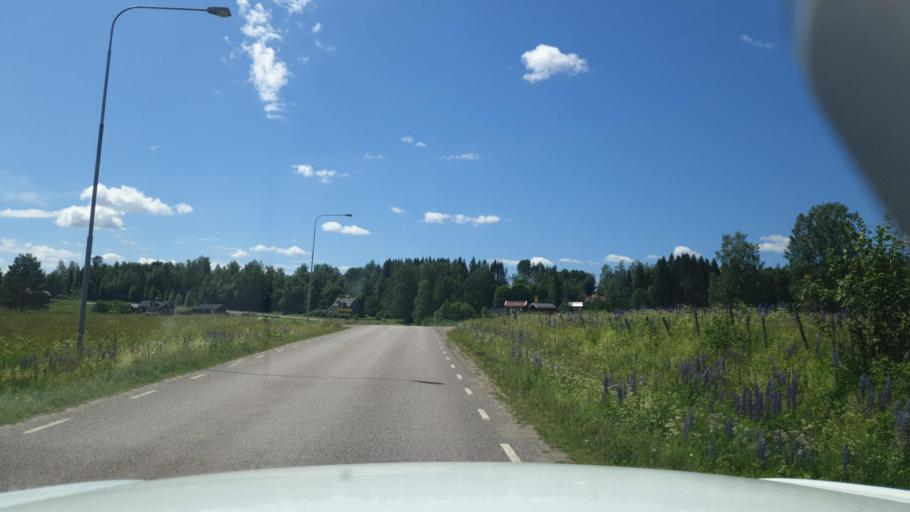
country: SE
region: Vaermland
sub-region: Eda Kommun
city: Charlottenberg
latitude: 59.9642
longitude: 12.4009
